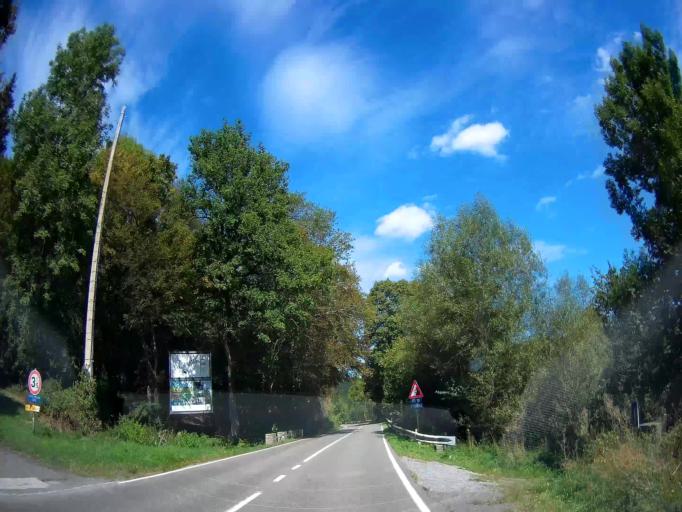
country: BE
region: Wallonia
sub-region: Province du Luxembourg
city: Rendeux
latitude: 50.2034
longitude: 5.5345
